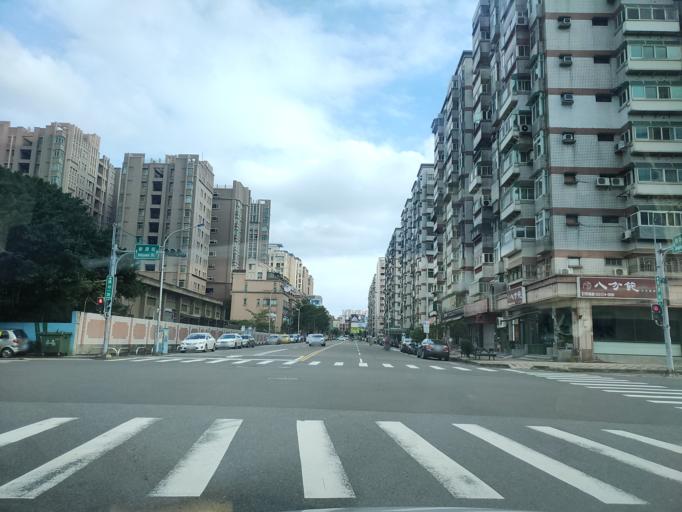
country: TW
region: Taiwan
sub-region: Hsinchu
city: Hsinchu
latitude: 24.8031
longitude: 120.9932
